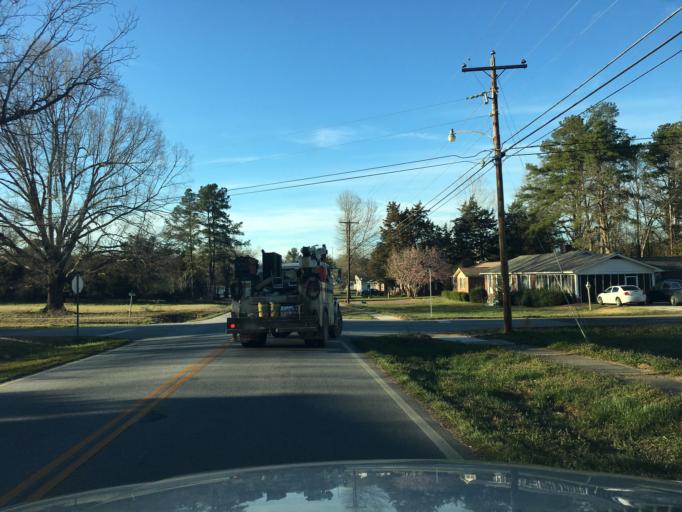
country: US
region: South Carolina
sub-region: Saluda County
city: Saluda
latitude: 34.0101
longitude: -81.7761
